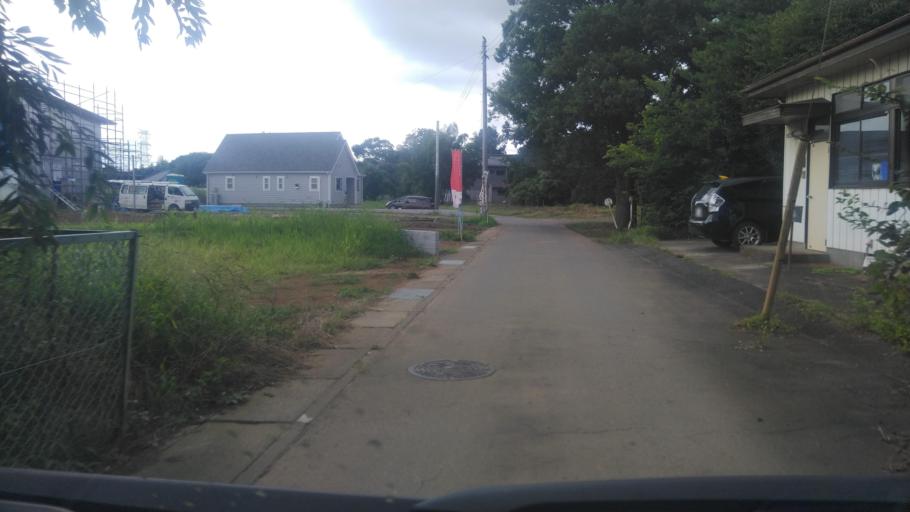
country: JP
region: Ibaraki
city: Ushiku
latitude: 36.0129
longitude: 140.1353
